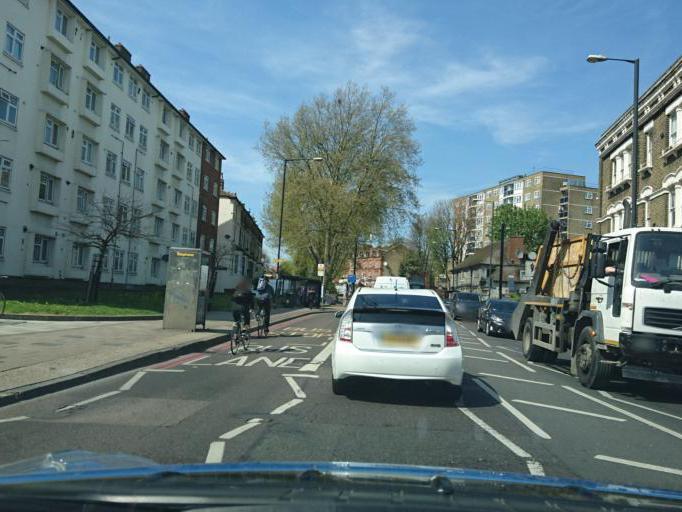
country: GB
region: England
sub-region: Greater London
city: Hackney
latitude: 51.5614
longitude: -0.0572
